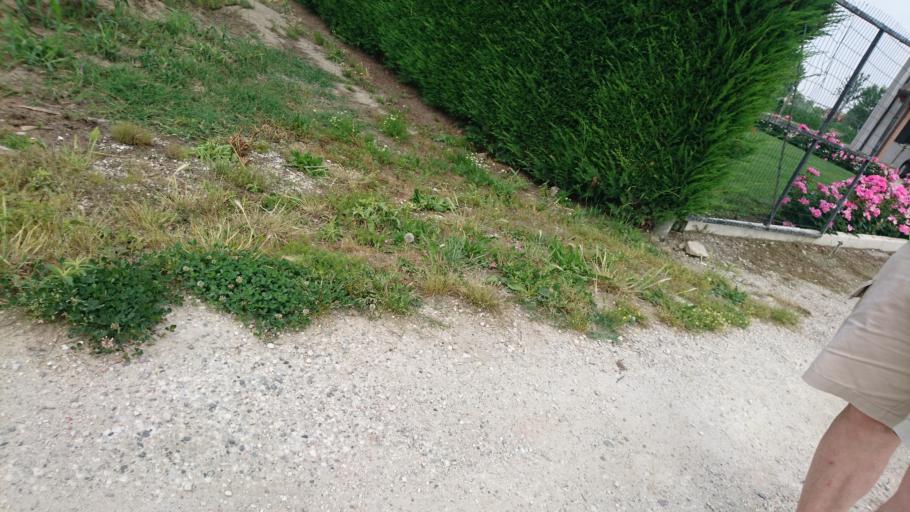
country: IT
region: Veneto
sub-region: Provincia di Padova
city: Terrassa Padovana
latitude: 45.2579
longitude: 11.8868
